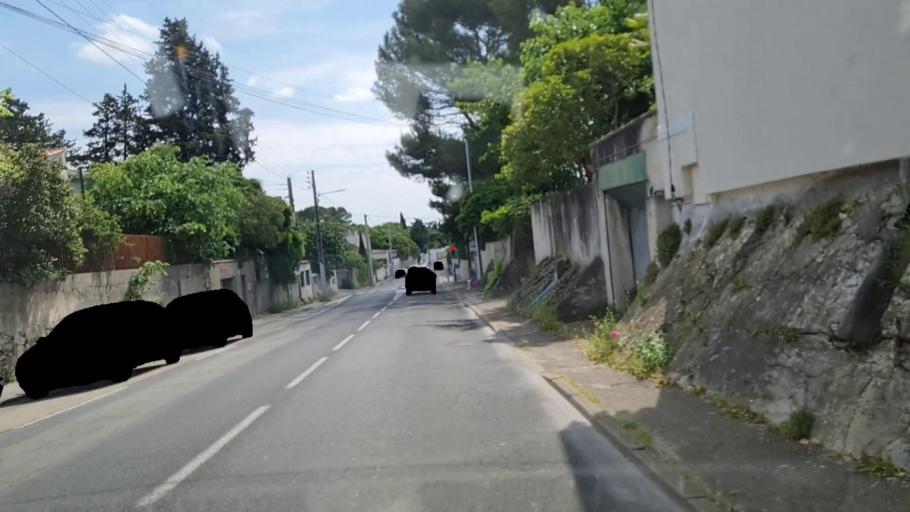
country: FR
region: Languedoc-Roussillon
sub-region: Departement du Gard
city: Nimes
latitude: 43.8375
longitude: 4.3281
